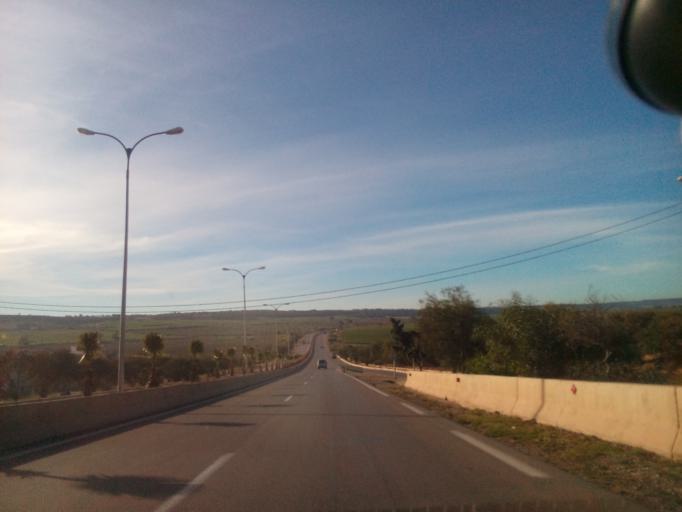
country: DZ
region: Mostaganem
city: Mostaganem
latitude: 35.8318
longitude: -0.0102
